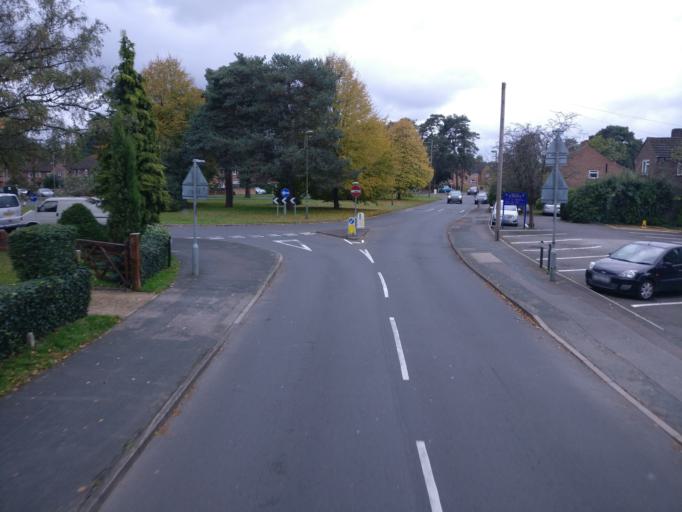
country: GB
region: England
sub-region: Surrey
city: Camberley
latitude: 51.3488
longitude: -0.7235
